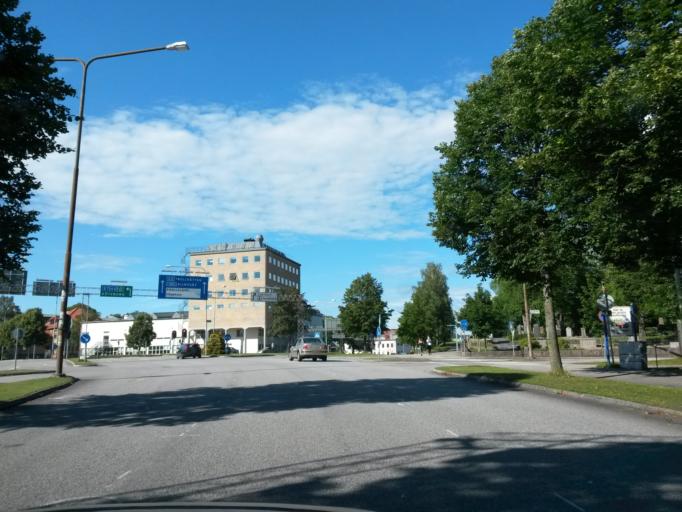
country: SE
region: Vaestra Goetaland
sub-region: Boras Kommun
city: Boras
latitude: 57.7176
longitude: 12.9327
